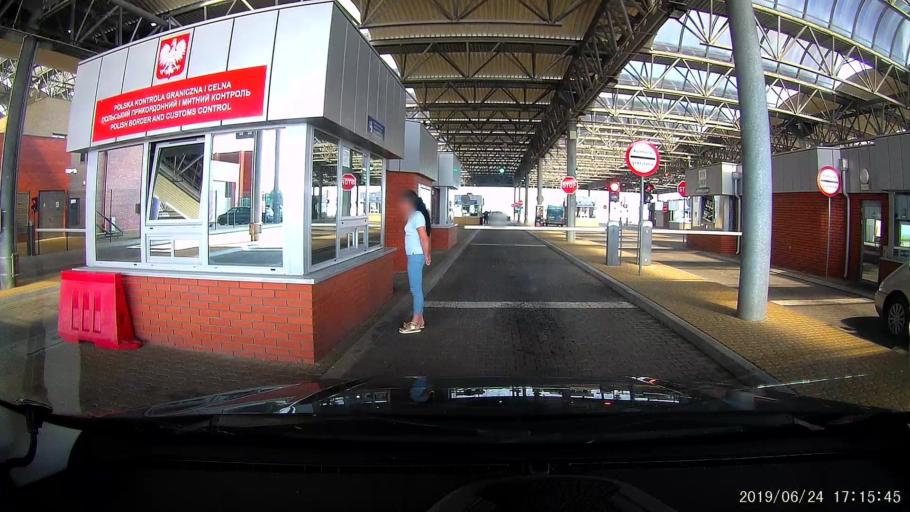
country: PL
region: Lublin Voivodeship
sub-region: Powiat hrubieszowski
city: Dolhobyczow
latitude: 50.5778
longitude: 24.0859
